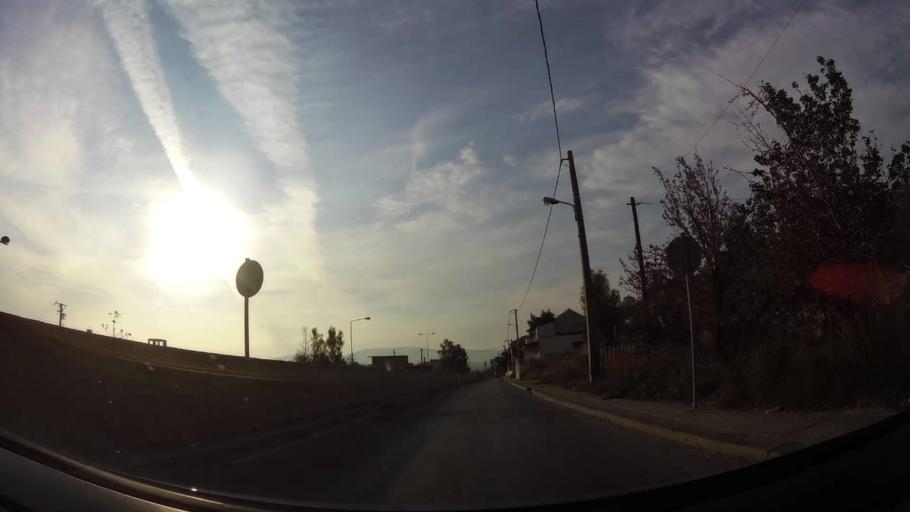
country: GR
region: Attica
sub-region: Nomarchia Dytikis Attikis
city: Zefyri
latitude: 38.0680
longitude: 23.7117
